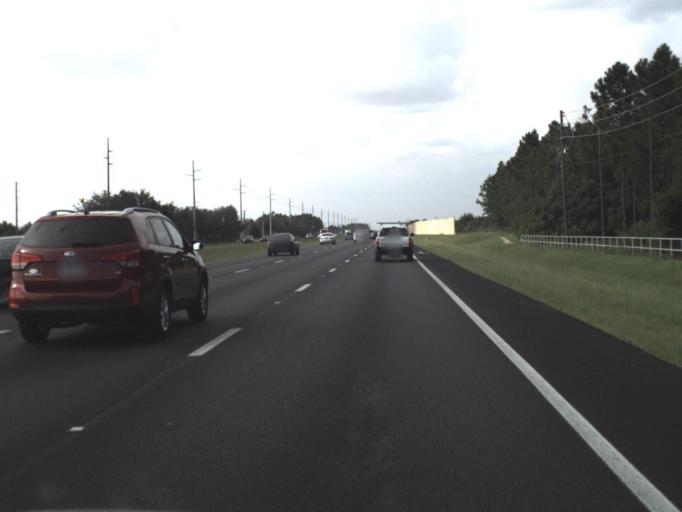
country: US
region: Florida
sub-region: Lake County
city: Four Corners
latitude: 28.2615
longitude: -81.6596
